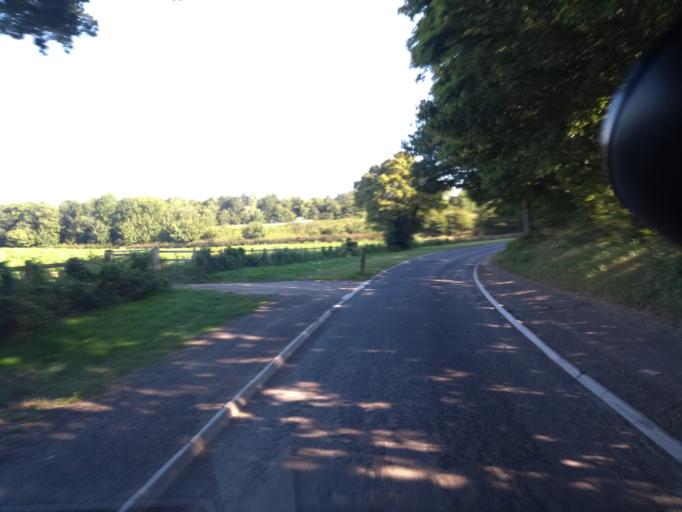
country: GB
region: England
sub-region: Somerset
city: South Petherton
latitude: 50.9375
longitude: -2.8253
